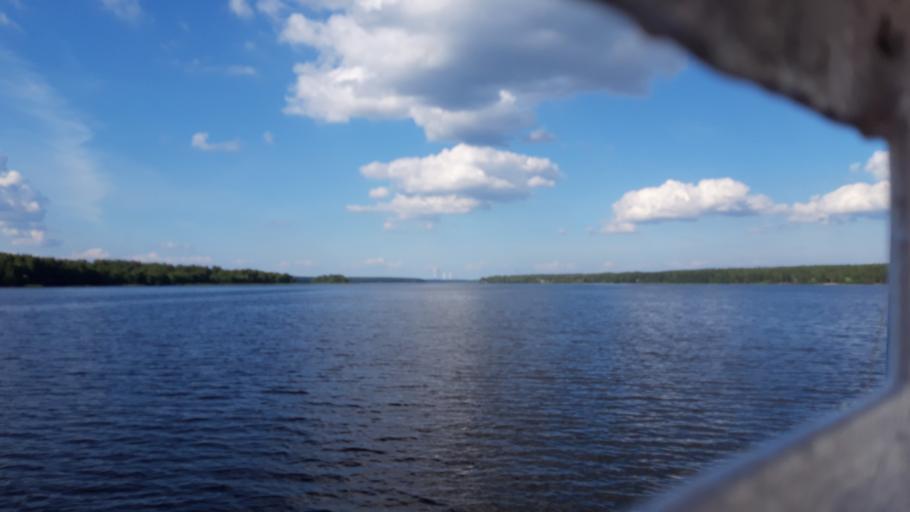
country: RU
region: Tverskaya
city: Konakovo
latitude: 56.6697
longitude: 36.6644
